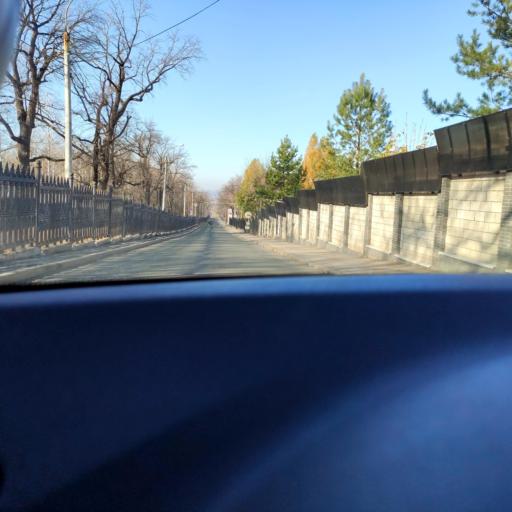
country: RU
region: Samara
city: Samara
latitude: 53.2304
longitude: 50.1696
